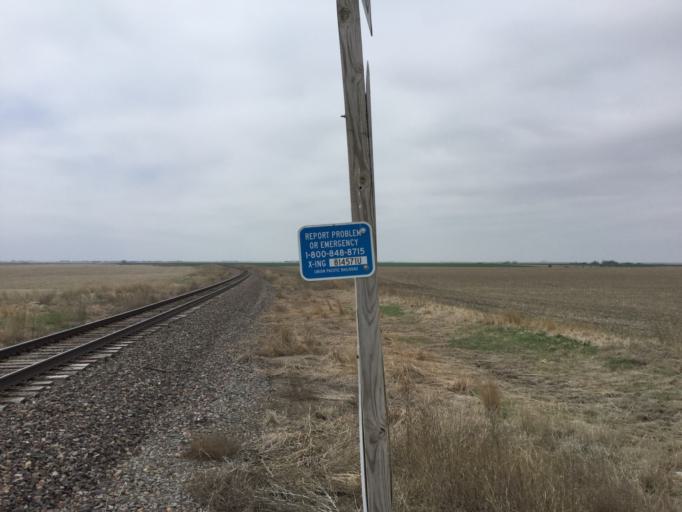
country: US
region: Kansas
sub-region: Russell County
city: Russell
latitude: 38.8771
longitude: -98.7252
